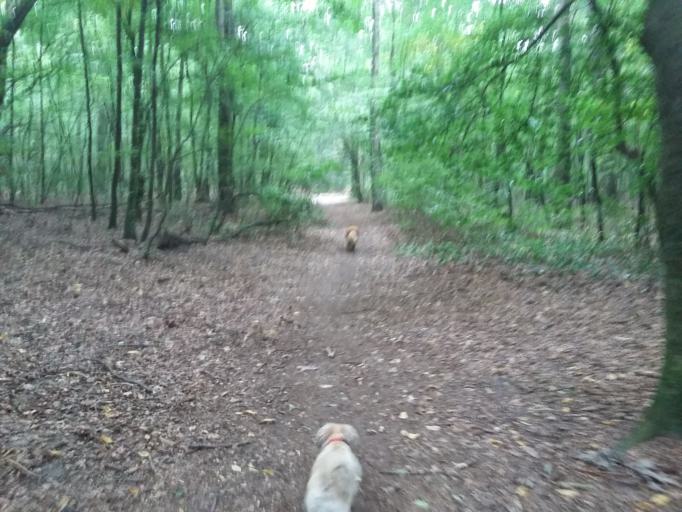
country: PL
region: Lodz Voivodeship
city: Lodz
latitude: 51.7616
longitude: 19.4190
